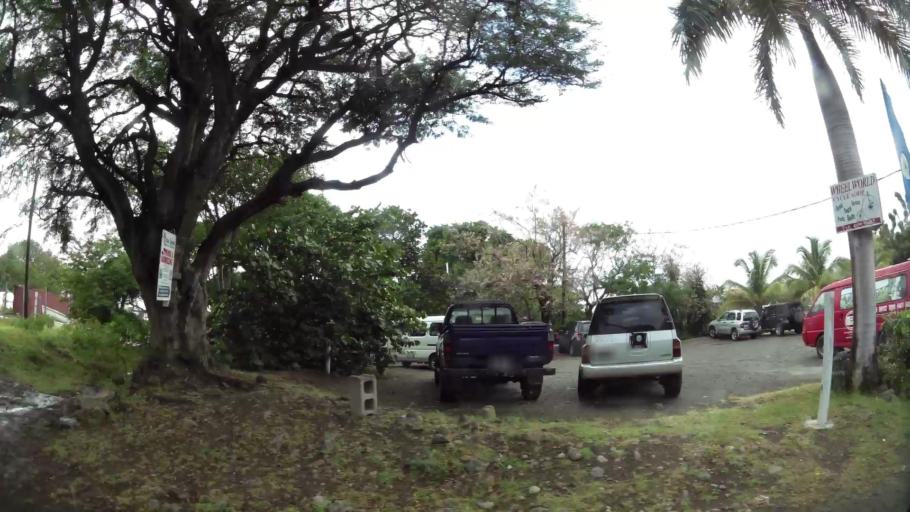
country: KN
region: Saint James Windwa
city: Newcastle
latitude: 17.1998
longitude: -62.6105
